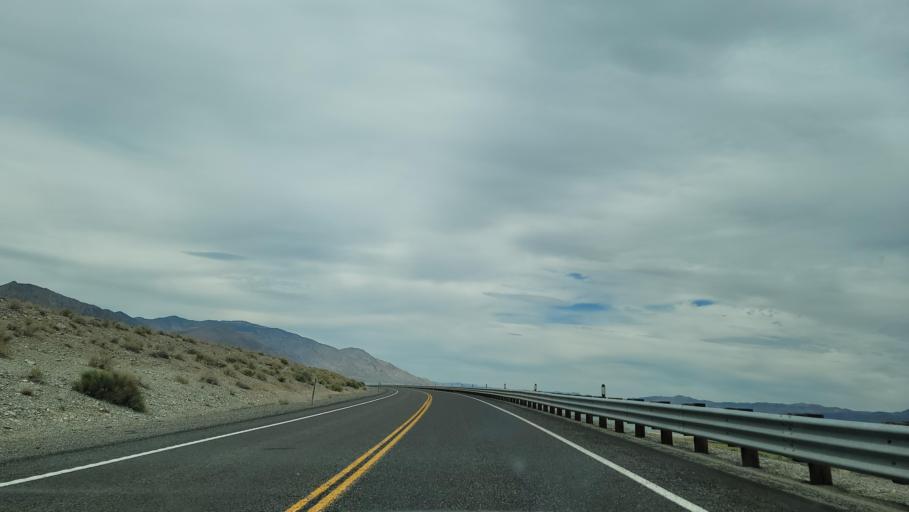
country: US
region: Nevada
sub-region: Mineral County
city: Hawthorne
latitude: 38.5972
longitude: -118.7076
